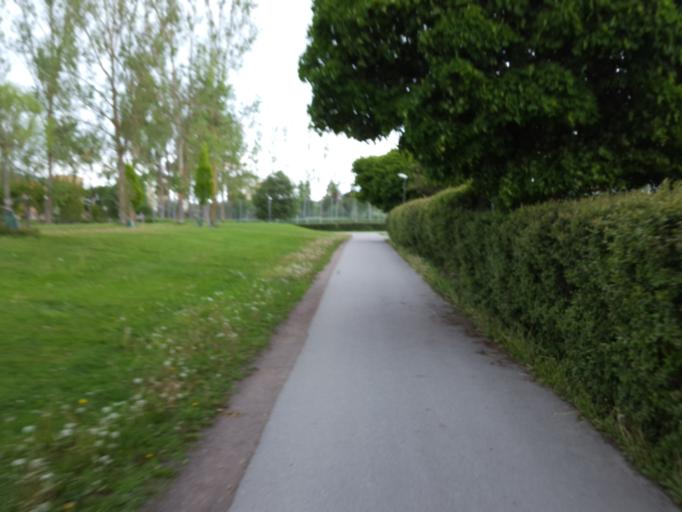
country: SE
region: Uppsala
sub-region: Uppsala Kommun
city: Gamla Uppsala
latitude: 59.8855
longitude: 17.6503
